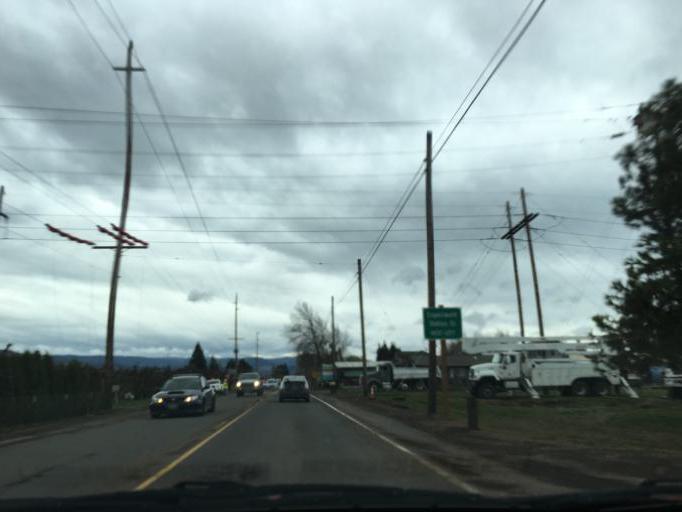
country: US
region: Oregon
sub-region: Hood River County
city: Hood River
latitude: 45.6884
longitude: -121.5237
